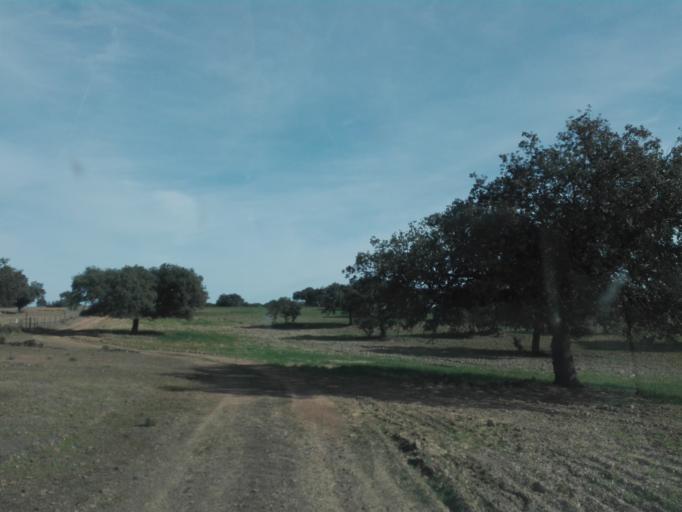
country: ES
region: Extremadura
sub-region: Provincia de Badajoz
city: Valverde de Llerena
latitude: 38.2183
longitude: -5.7428
